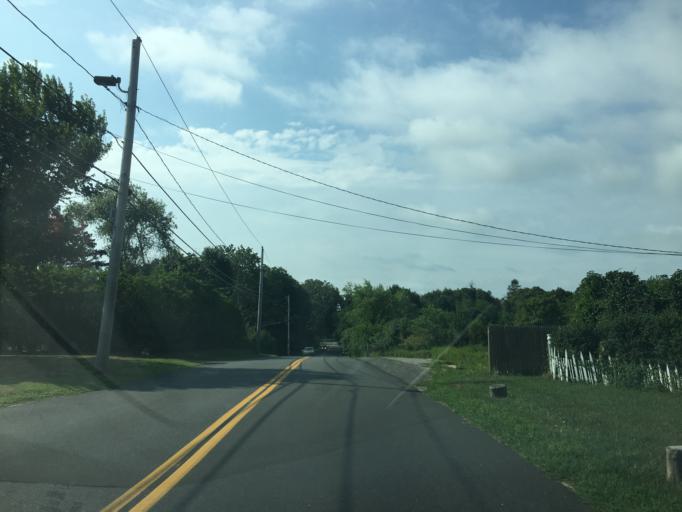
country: US
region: New York
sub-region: Suffolk County
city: Shelter Island
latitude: 41.0724
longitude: -72.3322
